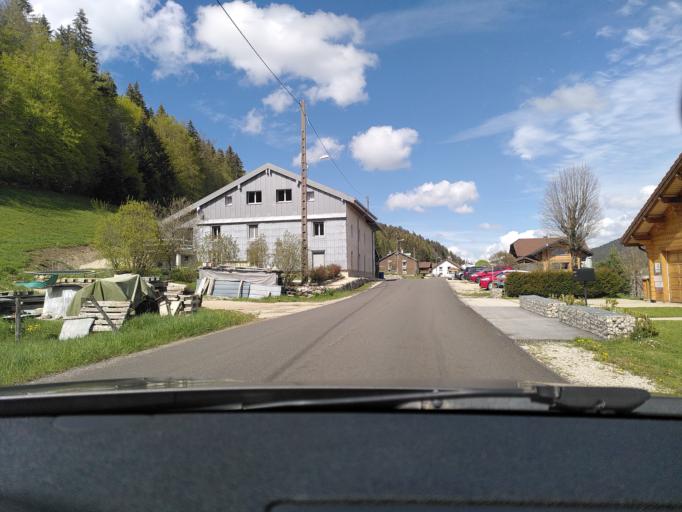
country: FR
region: Franche-Comte
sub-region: Departement du Jura
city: Les Rousses
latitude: 46.5282
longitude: 6.1193
